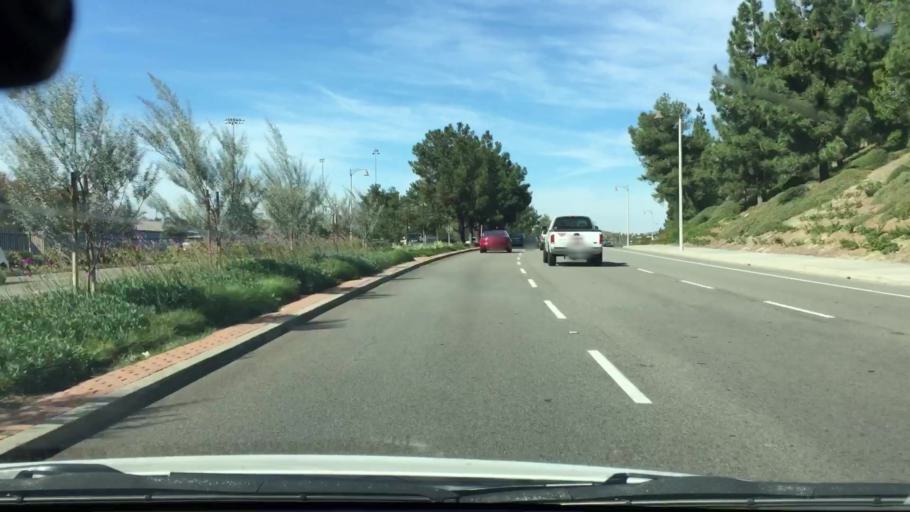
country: US
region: California
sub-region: Orange County
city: Portola Hills
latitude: 33.6548
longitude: -117.6491
